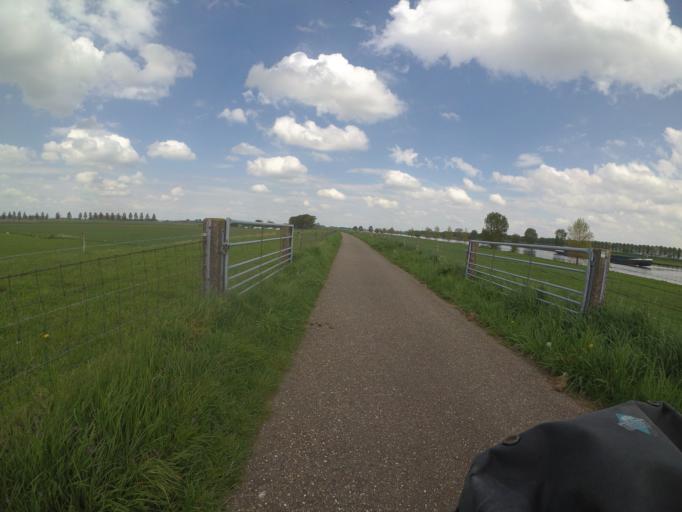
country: NL
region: North Brabant
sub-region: Gemeente Waalwijk
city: Waalwijk
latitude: 51.7168
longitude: 5.0660
